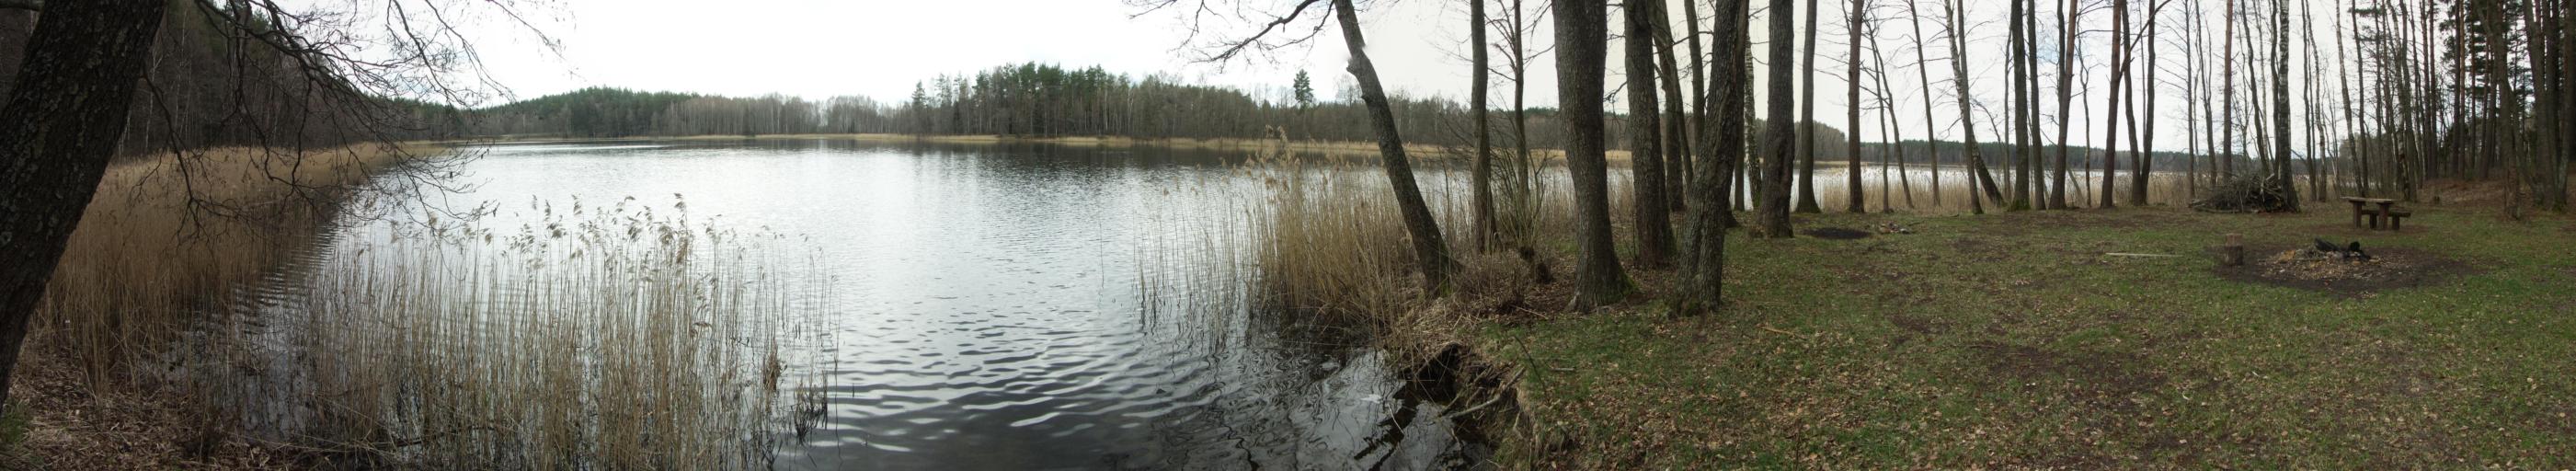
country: LT
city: Svencioneliai
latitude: 55.3292
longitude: 25.8257
